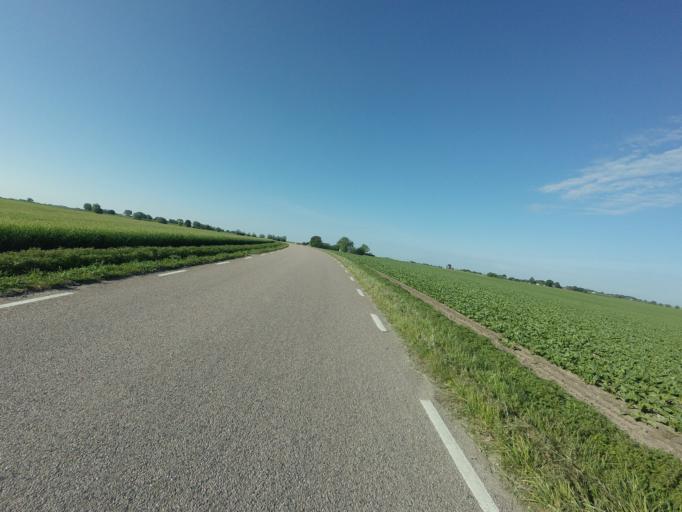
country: SE
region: Skane
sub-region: Malmo
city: Oxie
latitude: 55.4598
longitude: 13.1244
